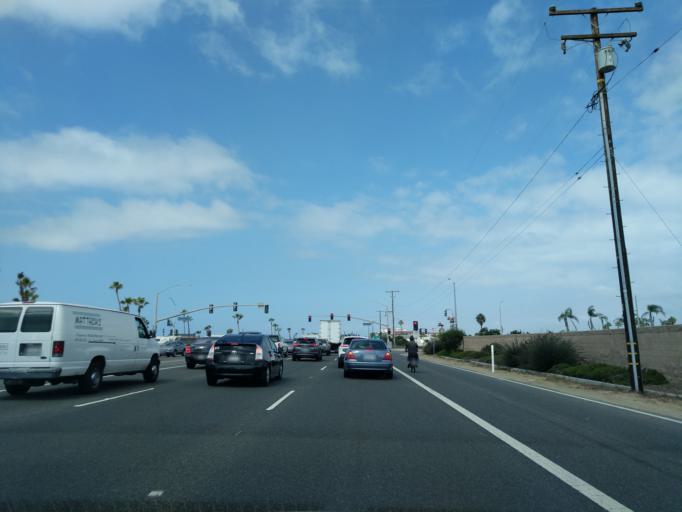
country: US
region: California
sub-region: Orange County
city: Huntington Beach
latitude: 33.6439
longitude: -117.9803
